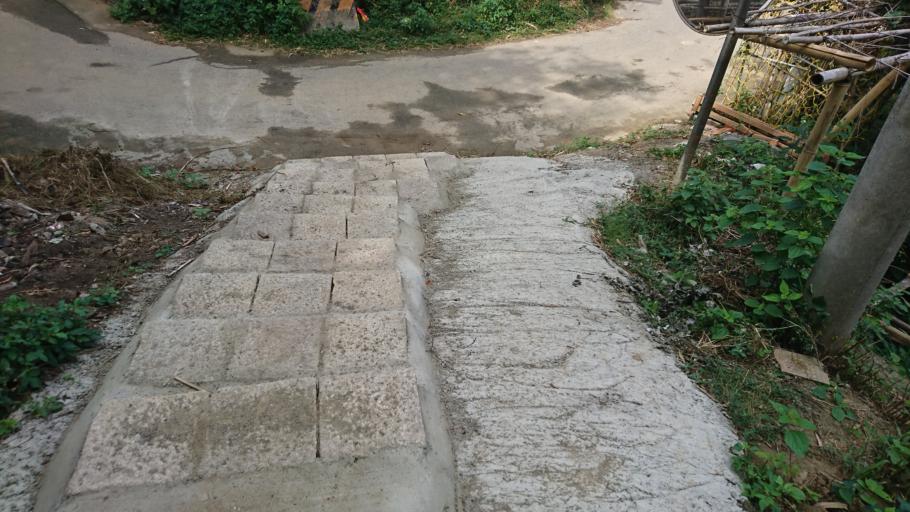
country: TW
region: Taiwan
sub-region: Miaoli
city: Miaoli
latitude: 24.5740
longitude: 120.8523
